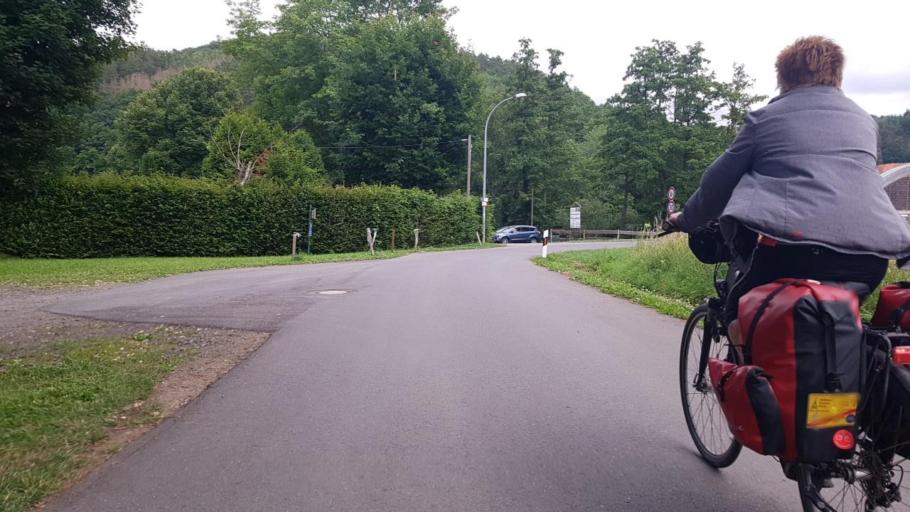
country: DE
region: North Rhine-Westphalia
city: Heimbach
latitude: 50.6541
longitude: 6.4917
